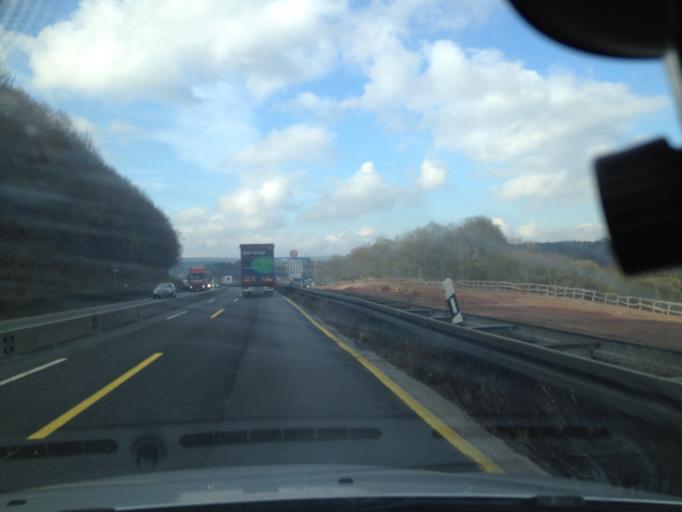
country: DE
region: Bavaria
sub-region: Regierungsbezirk Unterfranken
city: Marktheidenfeld
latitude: 49.7674
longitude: 9.5971
